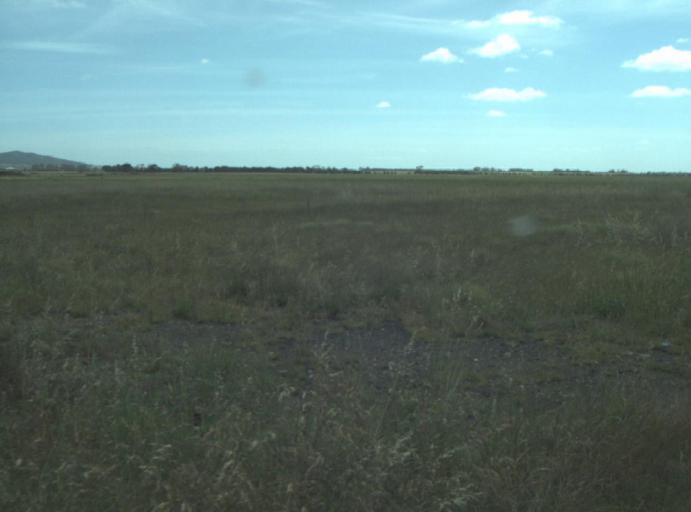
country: AU
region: Victoria
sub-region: Greater Geelong
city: Lara
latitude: -38.0123
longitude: 144.4553
